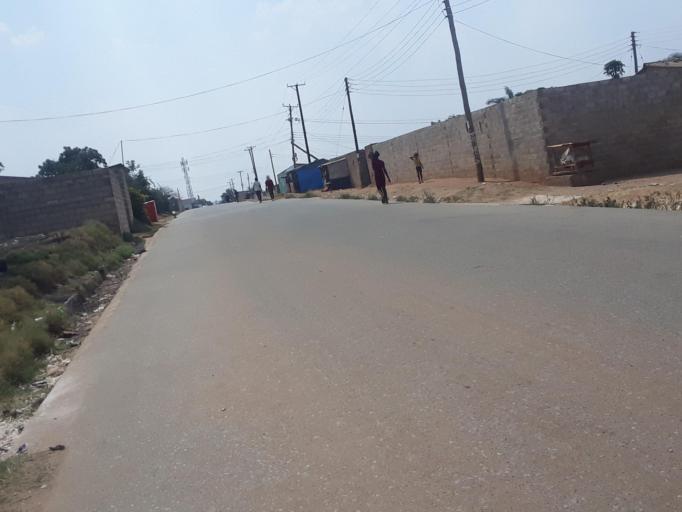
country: ZM
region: Lusaka
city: Lusaka
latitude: -15.3610
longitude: 28.3027
